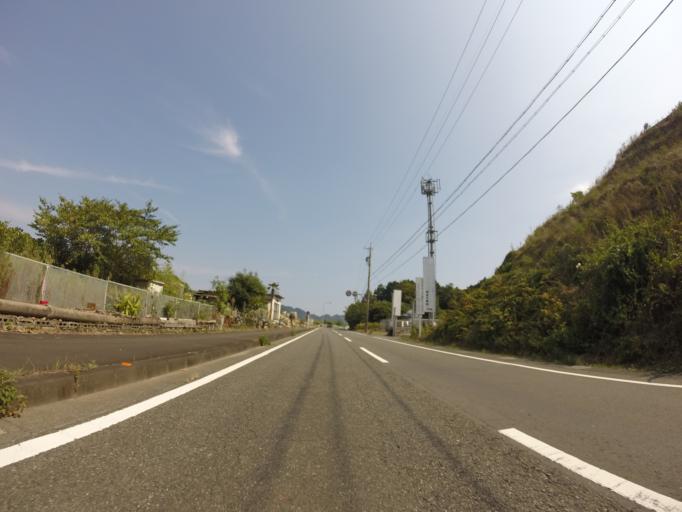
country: JP
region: Shizuoka
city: Shizuoka-shi
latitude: 35.0525
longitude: 138.3655
